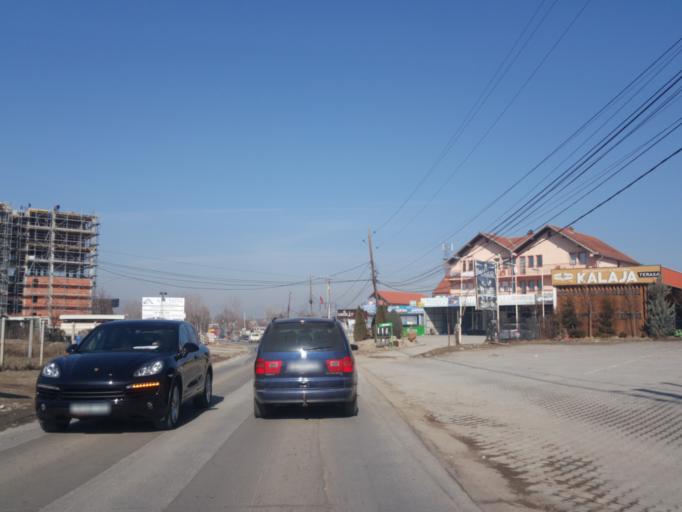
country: XK
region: Mitrovica
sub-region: Vushtrri
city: Vushtrri
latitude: 42.8184
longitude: 20.9818
